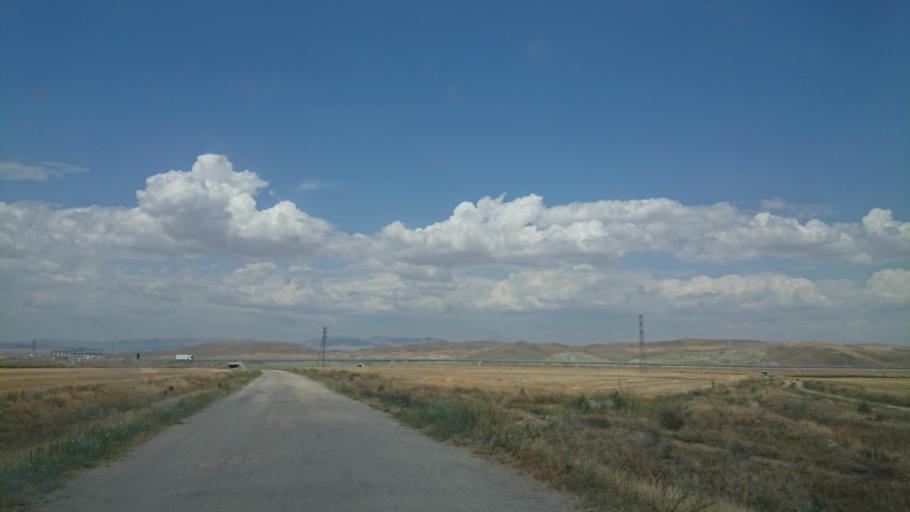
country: TR
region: Aksaray
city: Sariyahsi
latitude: 38.9705
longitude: 33.8984
